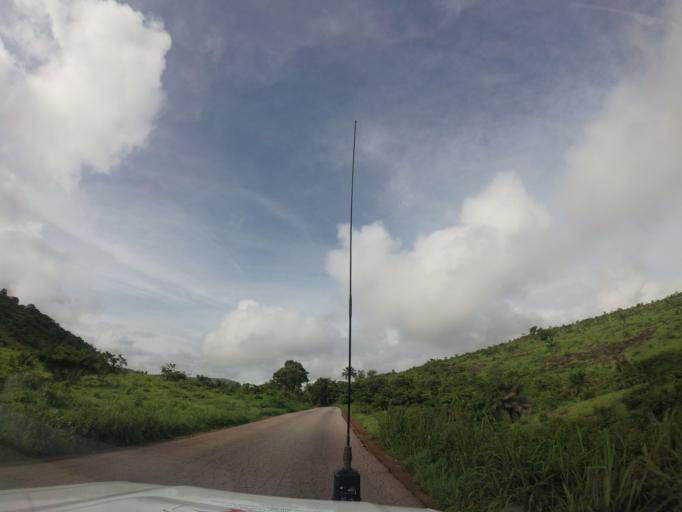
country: GN
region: Kindia
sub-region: Coyah
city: Coyah
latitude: 9.8407
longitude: -13.1502
